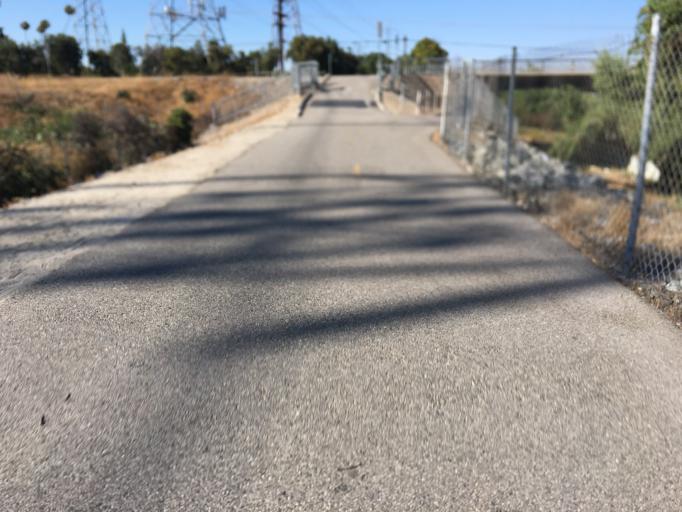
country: US
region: California
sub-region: Los Angeles County
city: Santa Fe Springs
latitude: 33.9394
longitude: -118.0998
